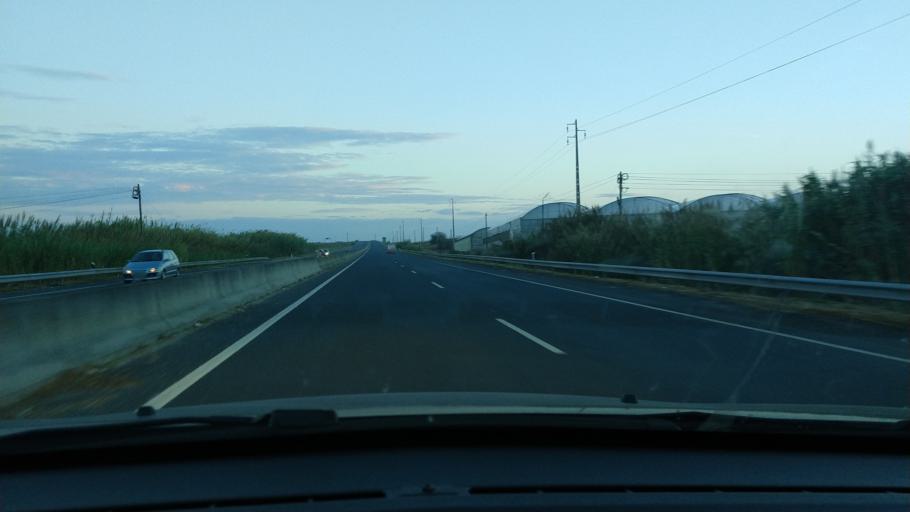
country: PT
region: Leiria
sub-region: Peniche
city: Atouguia da Baleia
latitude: 39.3414
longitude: -9.3390
